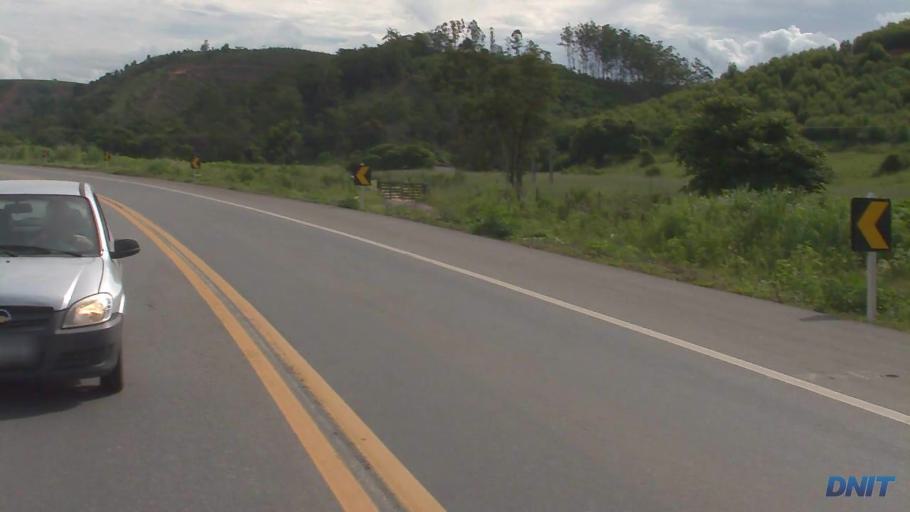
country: BR
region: Minas Gerais
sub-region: Belo Oriente
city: Belo Oriente
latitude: -19.2731
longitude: -42.3567
